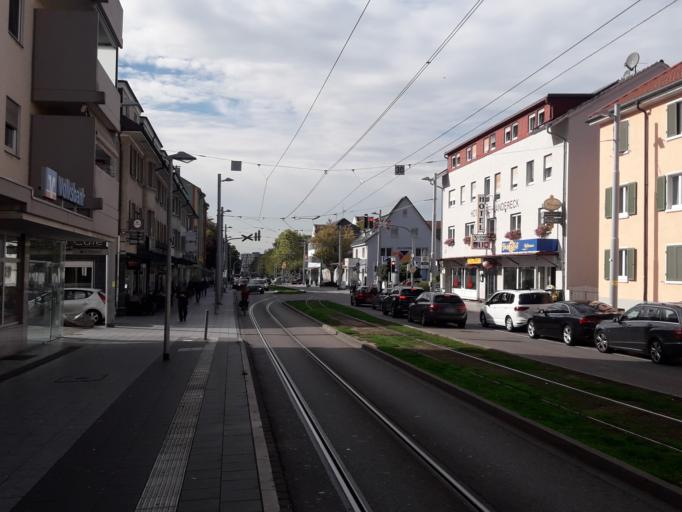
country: DE
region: Baden-Wuerttemberg
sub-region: Freiburg Region
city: Weil am Rhein
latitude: 47.5902
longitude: 7.5999
